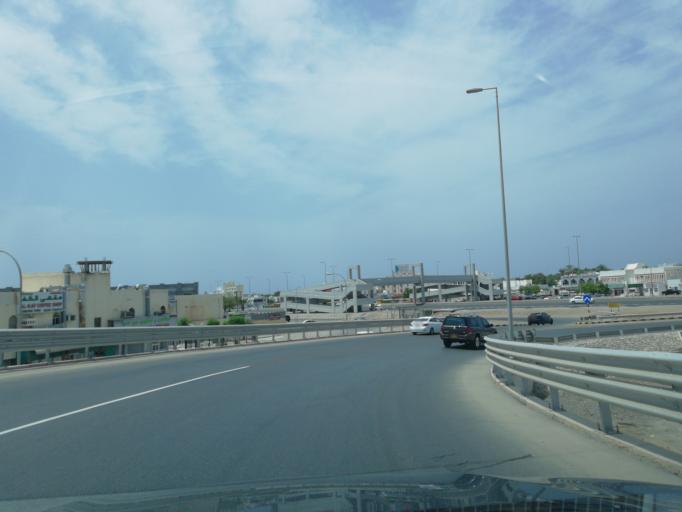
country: OM
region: Muhafazat Masqat
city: As Sib al Jadidah
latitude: 23.6741
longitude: 58.1370
